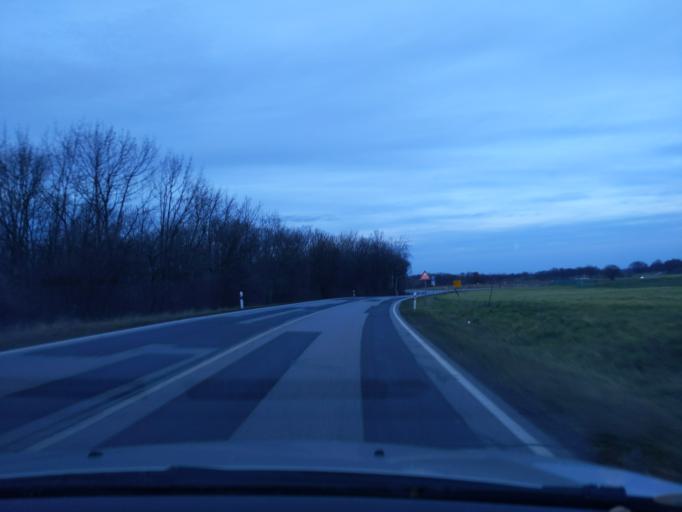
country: DE
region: Saxony
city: Grossdubrau
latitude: 51.2099
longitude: 14.4726
